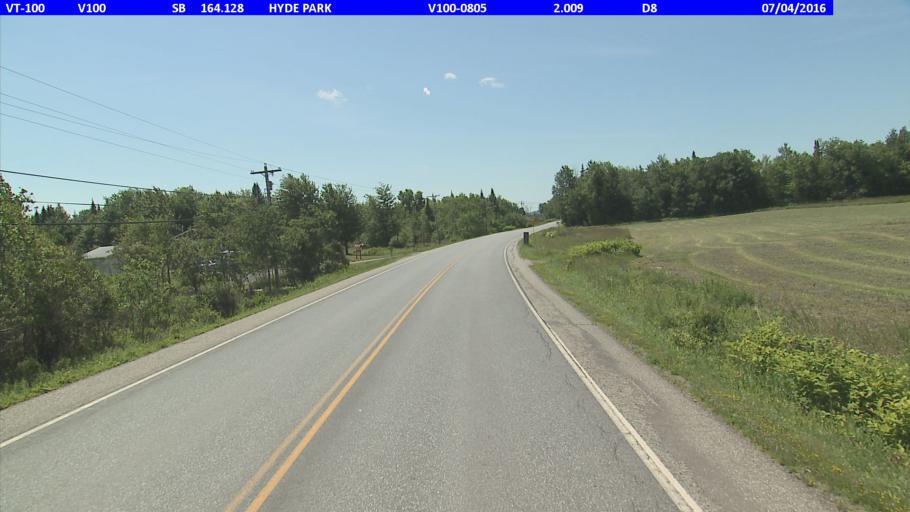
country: US
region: Vermont
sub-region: Lamoille County
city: Hyde Park
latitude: 44.6238
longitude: -72.5997
